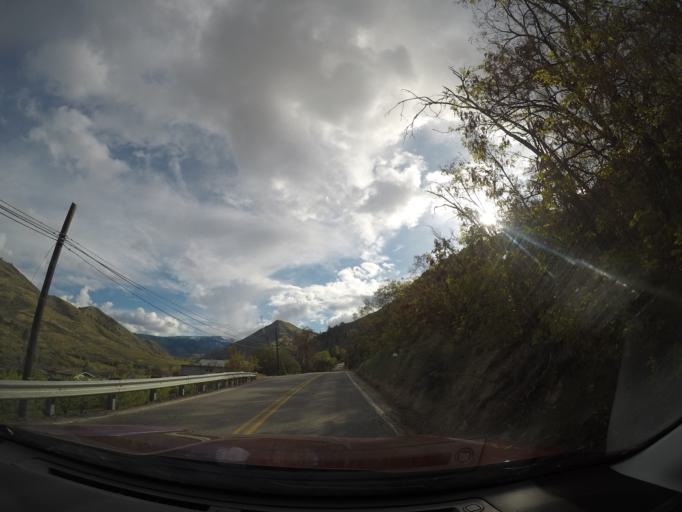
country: US
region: Washington
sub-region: Chelan County
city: South Wenatchee
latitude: 47.3823
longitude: -120.3133
